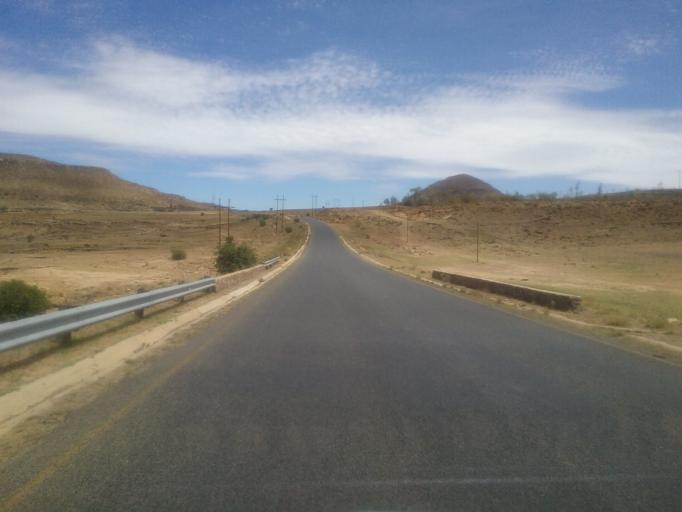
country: LS
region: Mafeteng
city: Mafeteng
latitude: -29.9635
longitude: 27.2998
